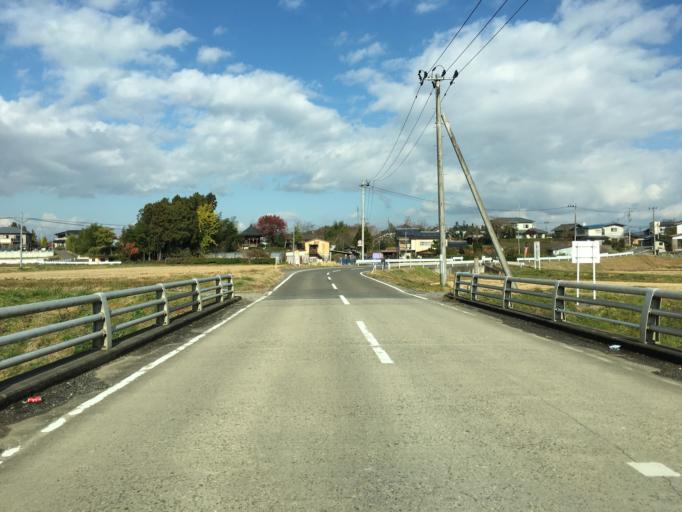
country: JP
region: Fukushima
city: Nihommatsu
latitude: 37.6475
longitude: 140.4817
